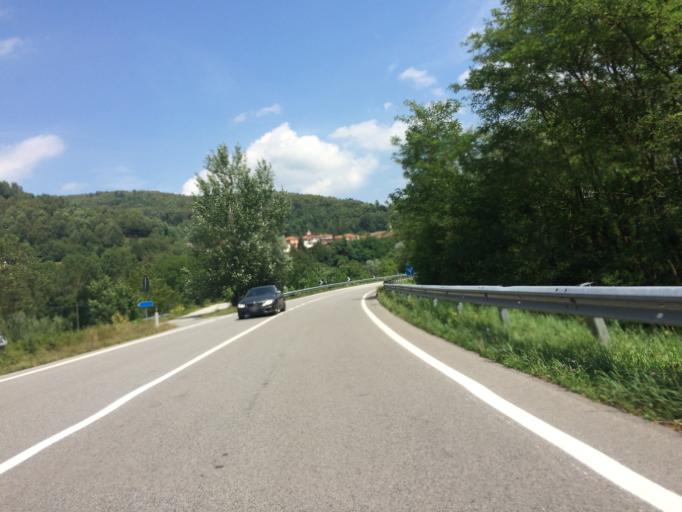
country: IT
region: Piedmont
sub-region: Provincia di Cuneo
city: Priola
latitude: 44.2370
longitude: 8.0152
